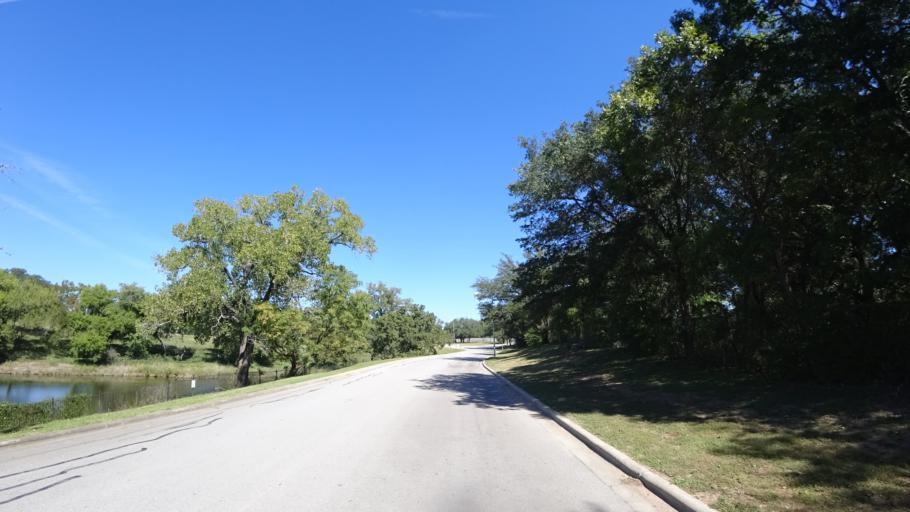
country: US
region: Texas
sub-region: Travis County
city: Hornsby Bend
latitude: 30.2752
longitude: -97.6385
